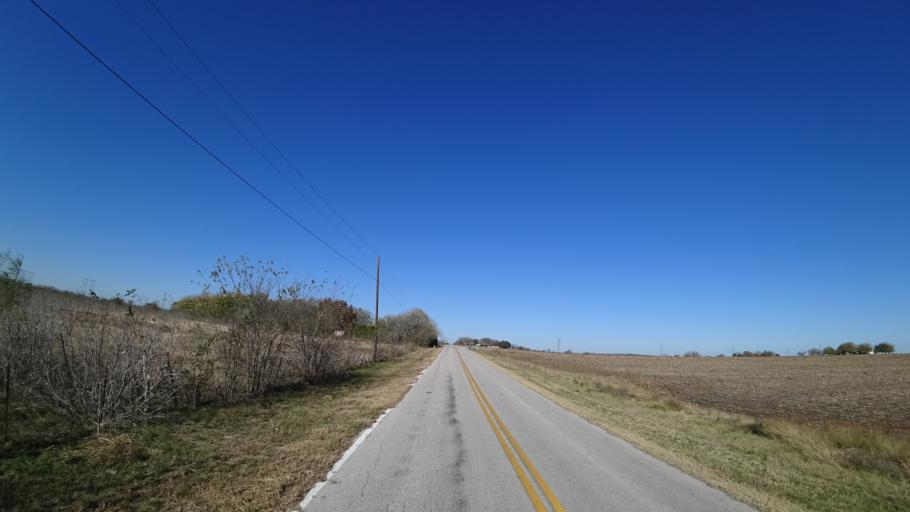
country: US
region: Texas
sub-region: Travis County
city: Onion Creek
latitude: 30.0963
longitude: -97.6615
